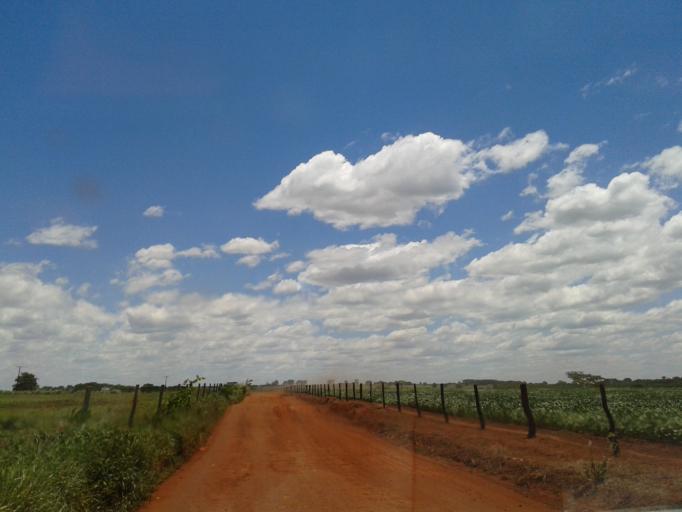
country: BR
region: Minas Gerais
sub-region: Centralina
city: Centralina
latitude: -18.7149
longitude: -49.2143
